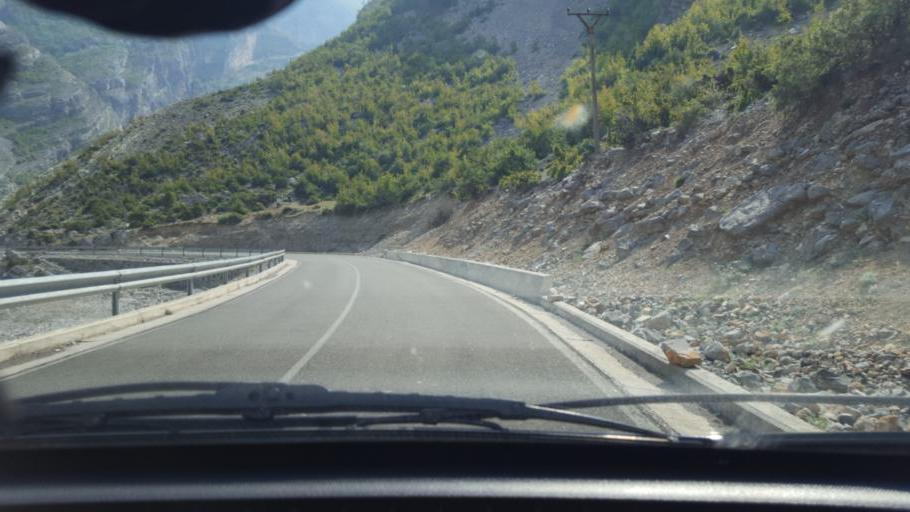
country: AL
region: Shkoder
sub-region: Rrethi i Malesia e Madhe
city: Kastrat
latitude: 42.4918
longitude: 19.5804
